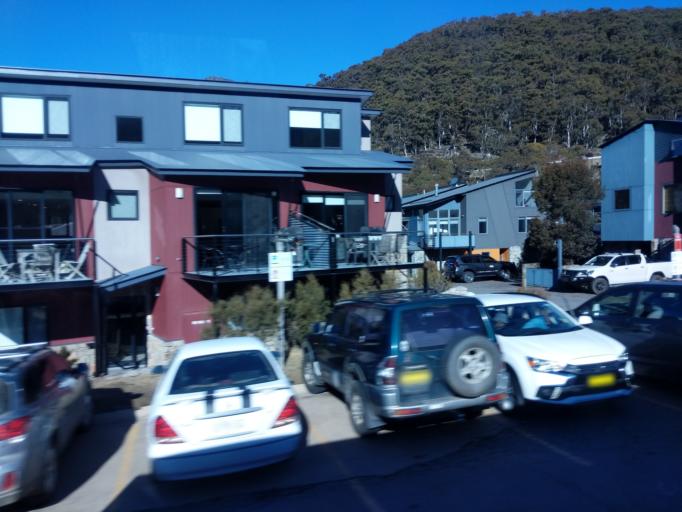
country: AU
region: New South Wales
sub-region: Snowy River
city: Jindabyne
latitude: -36.5000
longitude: 148.3110
